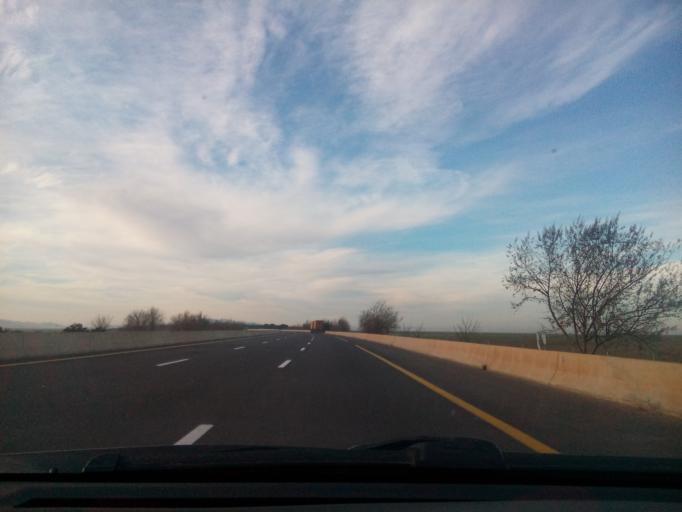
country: DZ
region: Mostaganem
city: Mostaganem
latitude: 35.6859
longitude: 0.1600
